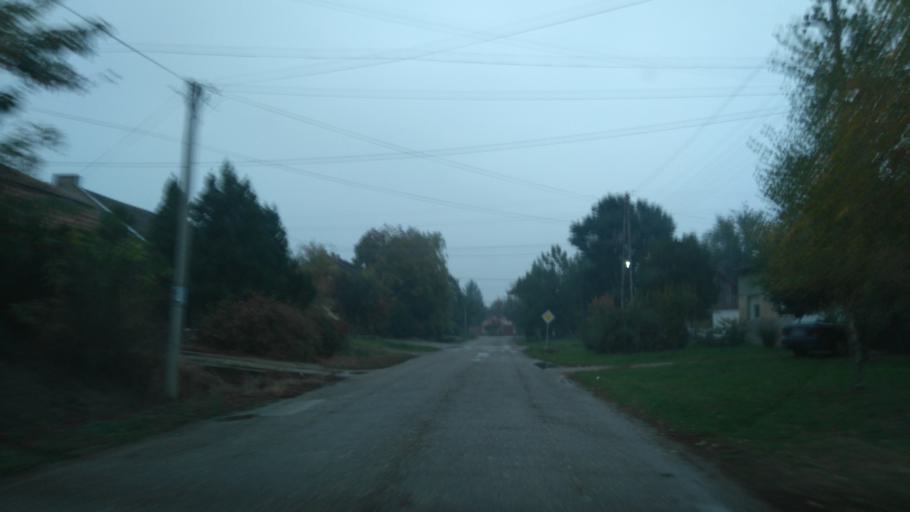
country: RS
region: Autonomna Pokrajina Vojvodina
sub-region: Juznobacki Okrug
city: Becej
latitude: 45.6238
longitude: 20.0449
